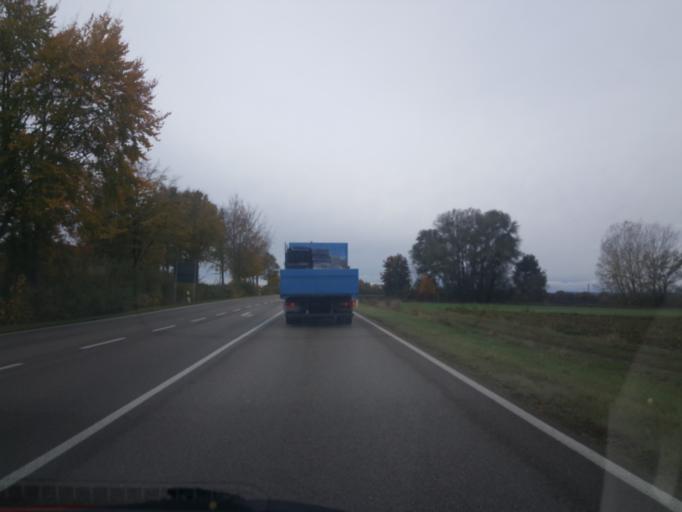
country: DE
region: Bavaria
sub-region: Upper Bavaria
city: Burgheim
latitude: 48.7098
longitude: 11.0053
